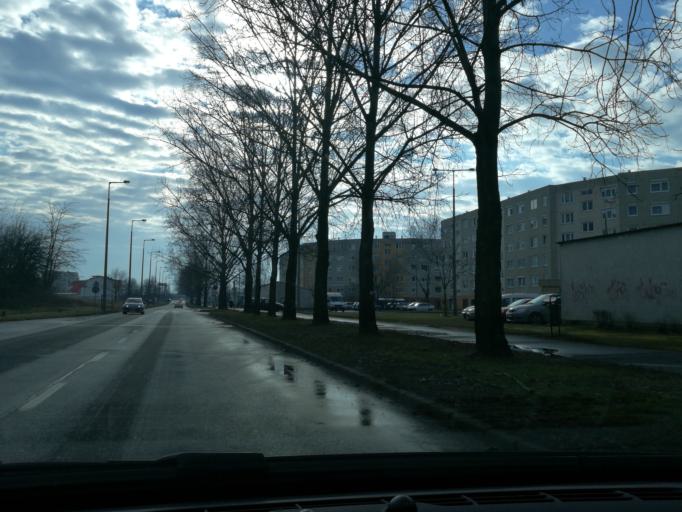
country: HU
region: Szabolcs-Szatmar-Bereg
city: Nyiregyhaza
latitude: 47.9589
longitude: 21.7439
